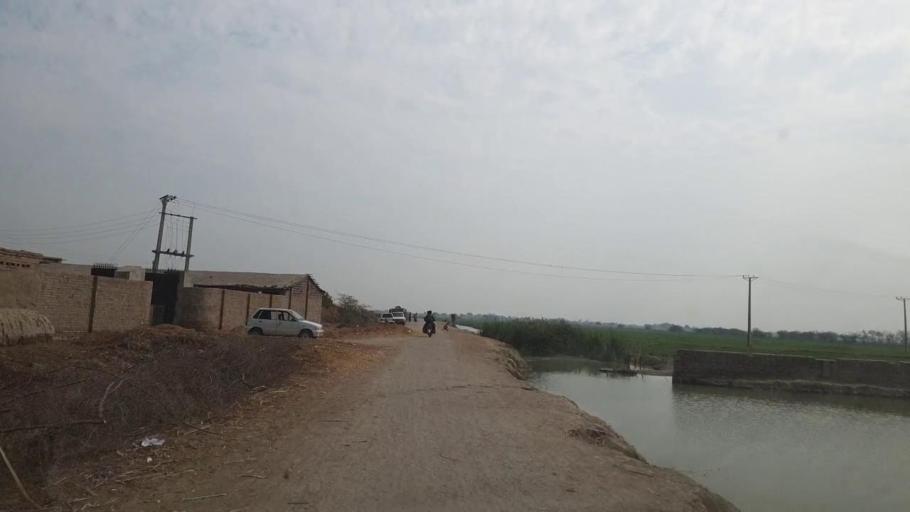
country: PK
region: Sindh
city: Mirpur Khas
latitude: 25.5362
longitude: 69.1306
